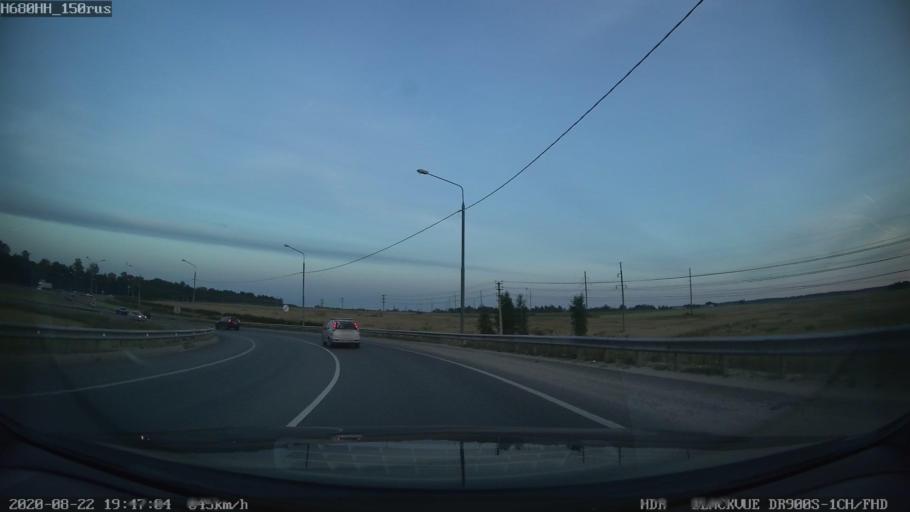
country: RU
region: Tverskaya
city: Emmaus
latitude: 56.7828
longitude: 36.0893
